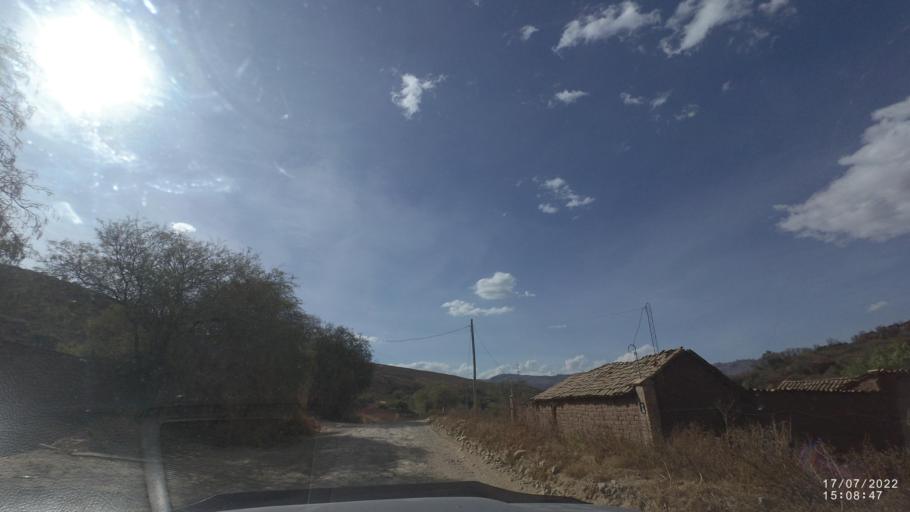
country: BO
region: Cochabamba
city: Capinota
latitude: -17.5779
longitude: -66.2666
